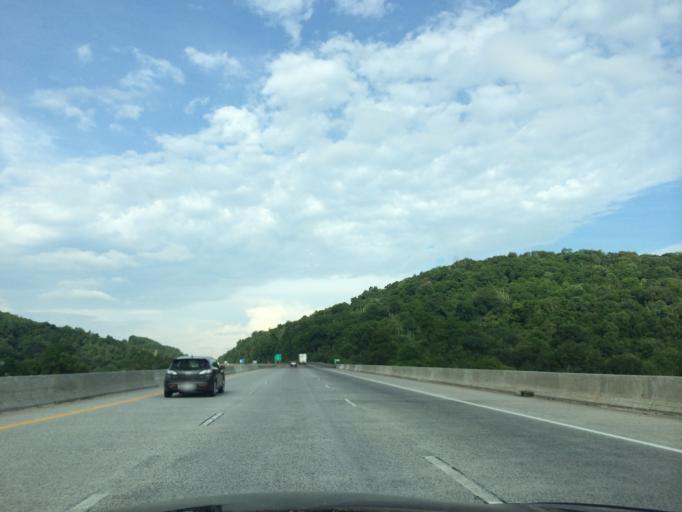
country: US
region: Maryland
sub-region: Allegany County
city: Frostburg
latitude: 39.6402
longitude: -78.8907
